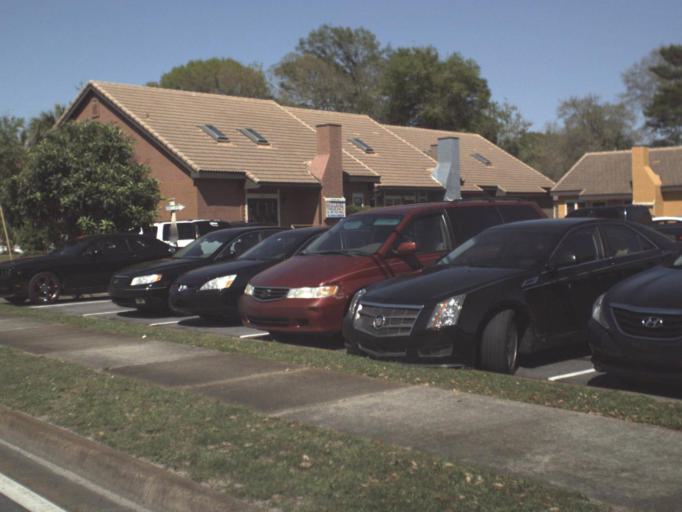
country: US
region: Florida
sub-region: Okaloosa County
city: Mary Esther
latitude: 30.4122
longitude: -86.6549
